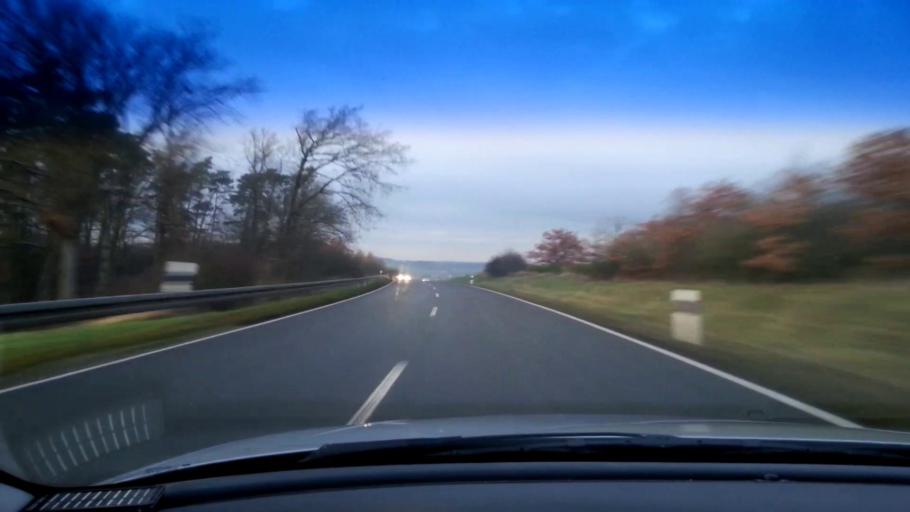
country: DE
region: Bavaria
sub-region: Upper Franconia
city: Frensdorf
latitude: 49.8097
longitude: 10.8379
